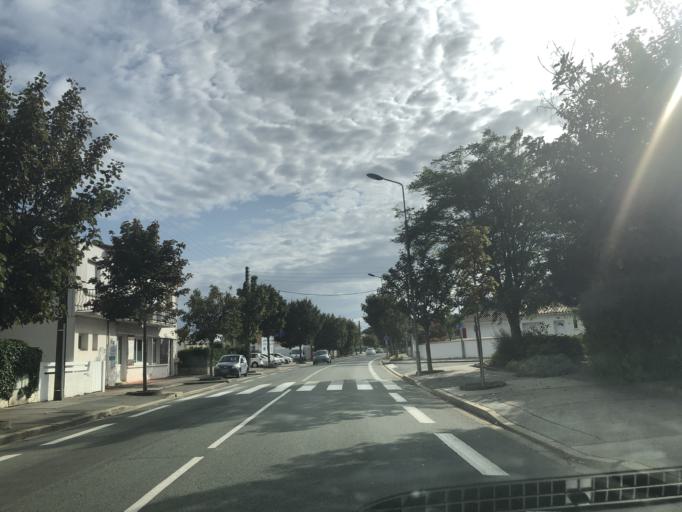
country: FR
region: Poitou-Charentes
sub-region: Departement de la Charente-Maritime
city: Royan
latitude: 45.6294
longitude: -1.0392
